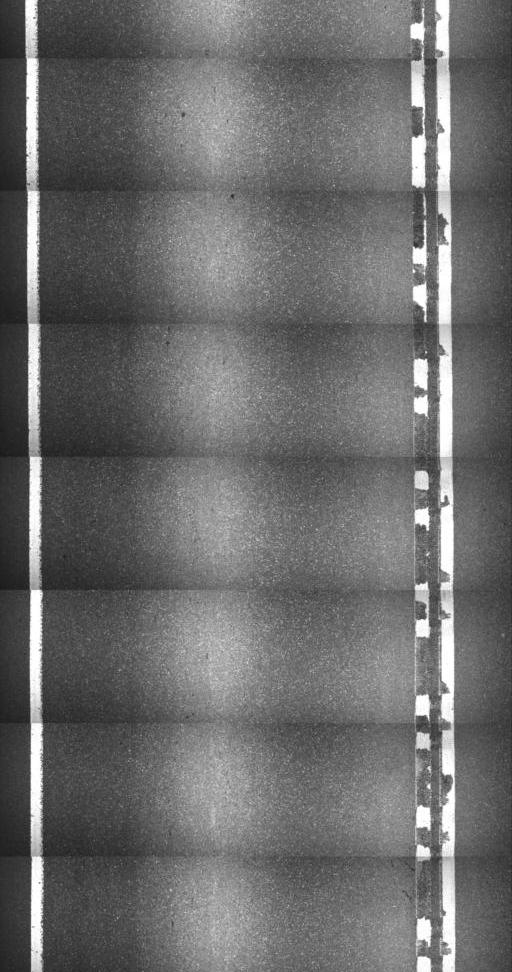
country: US
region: Vermont
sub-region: Washington County
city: Waterbury
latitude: 44.2189
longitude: -72.7908
